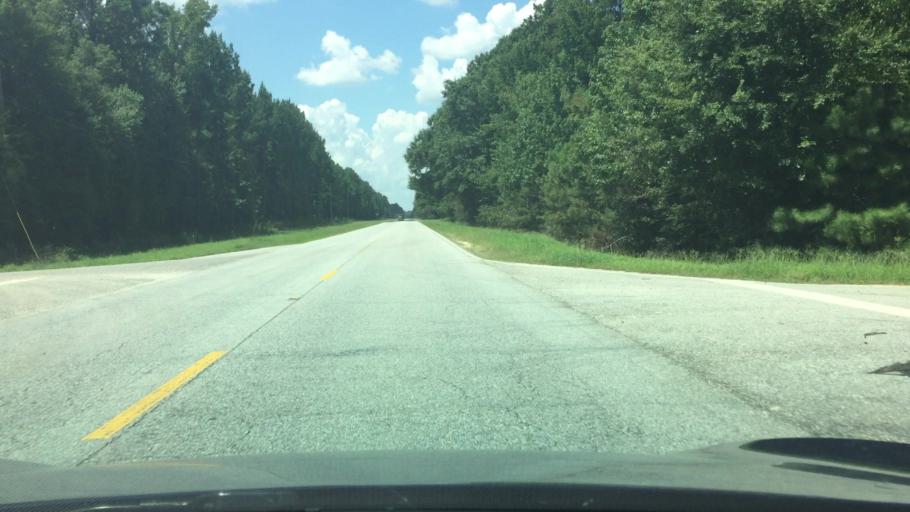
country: US
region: Alabama
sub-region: Montgomery County
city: Pike Road
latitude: 32.3900
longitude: -85.9796
